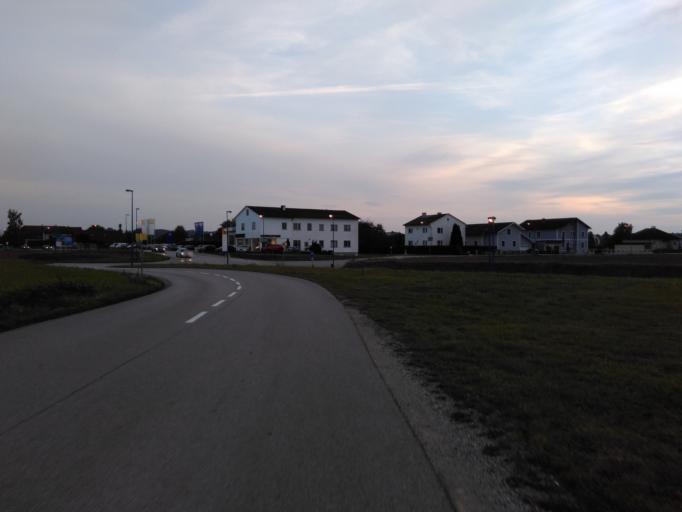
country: AT
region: Lower Austria
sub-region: Politischer Bezirk Amstetten
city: Sankt Valentin
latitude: 48.1668
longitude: 14.5161
